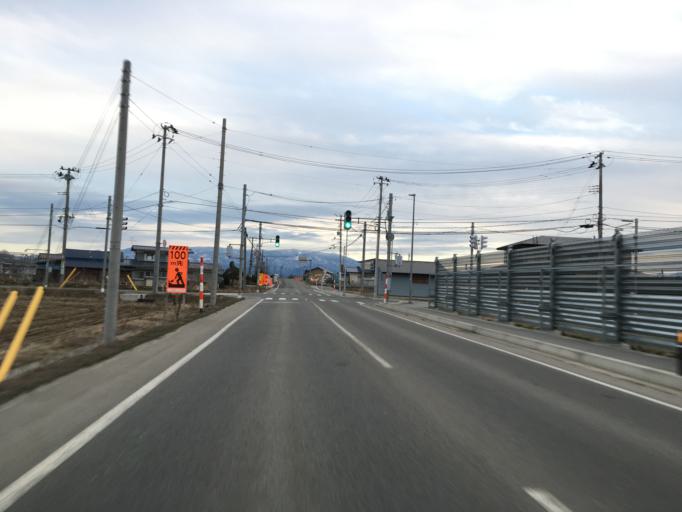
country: JP
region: Yamagata
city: Yonezawa
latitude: 37.9978
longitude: 140.0766
